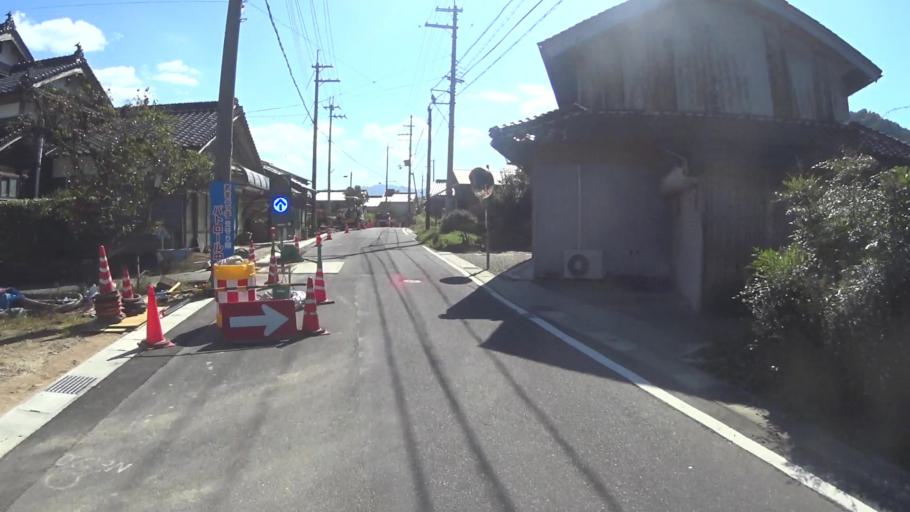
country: JP
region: Hyogo
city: Toyooka
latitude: 35.5882
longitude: 134.9248
